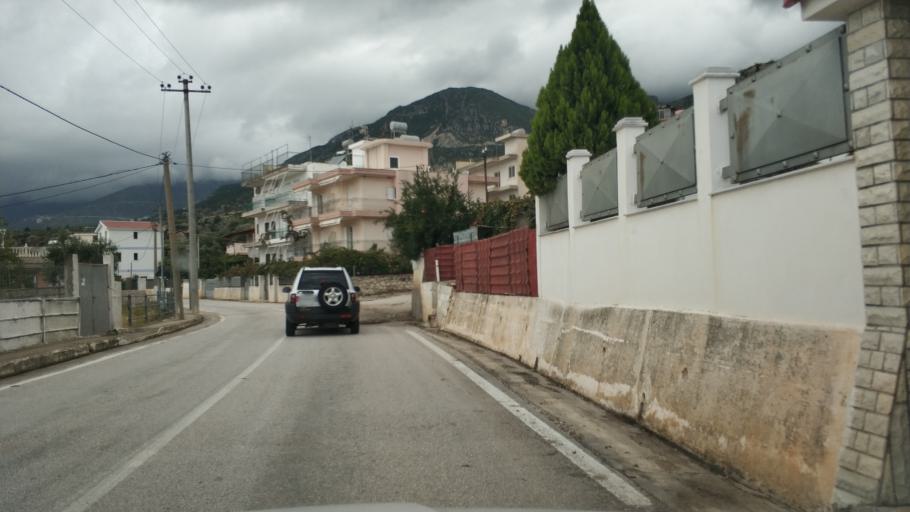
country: AL
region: Vlore
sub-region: Rrethi i Vlores
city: Vranisht
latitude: 40.1495
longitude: 19.6421
